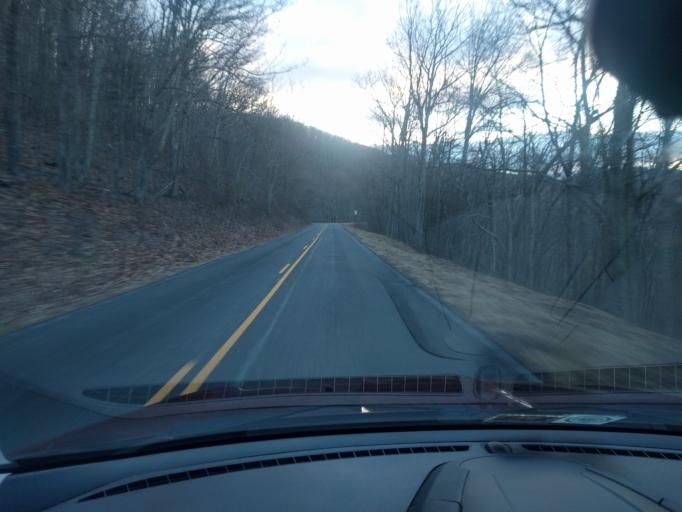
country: US
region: Virginia
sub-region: Botetourt County
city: Buchanan
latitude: 37.4803
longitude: -79.6572
